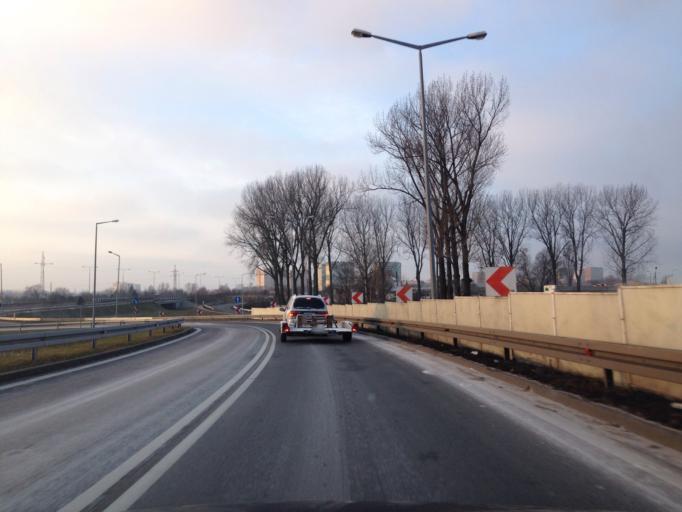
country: PL
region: Greater Poland Voivodeship
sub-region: Powiat gnieznienski
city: Gniezno
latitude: 52.5544
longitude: 17.6214
